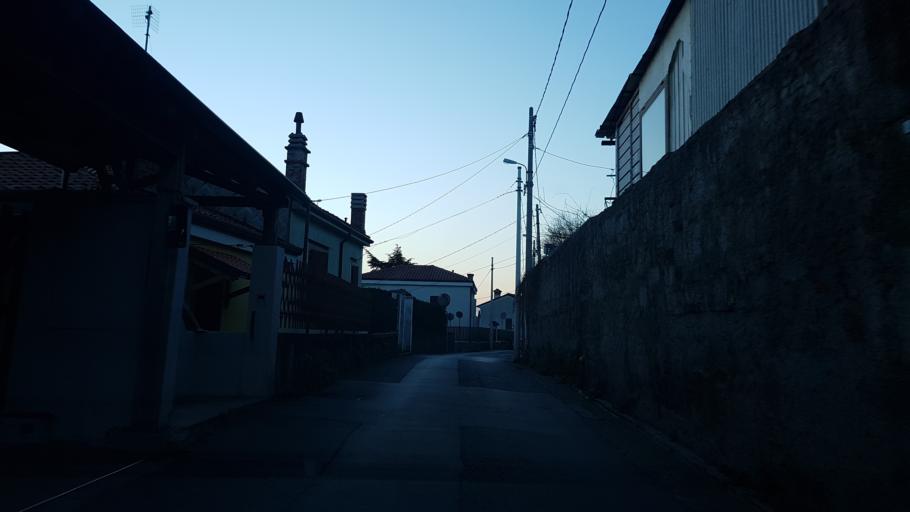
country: IT
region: Friuli Venezia Giulia
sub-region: Provincia di Trieste
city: Trieste
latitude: 45.6349
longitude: 13.8011
